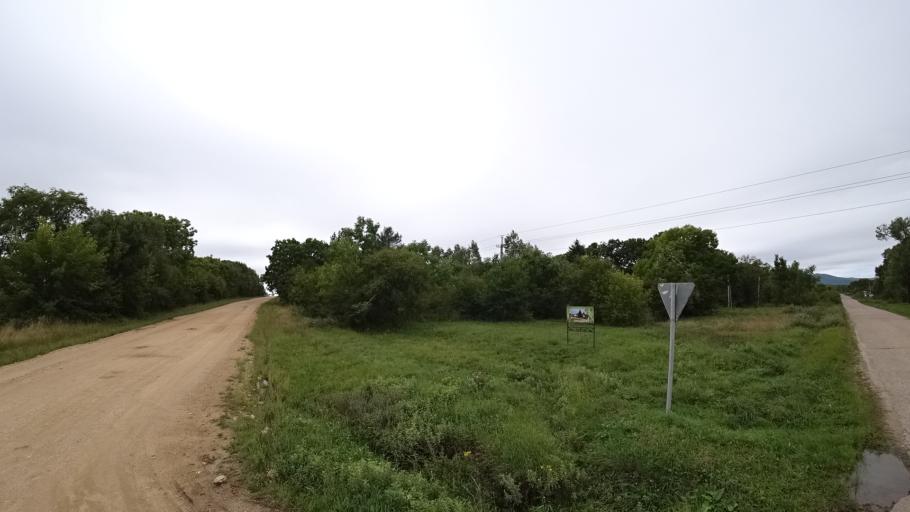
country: RU
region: Primorskiy
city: Monastyrishche
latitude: 44.0807
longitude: 132.5933
